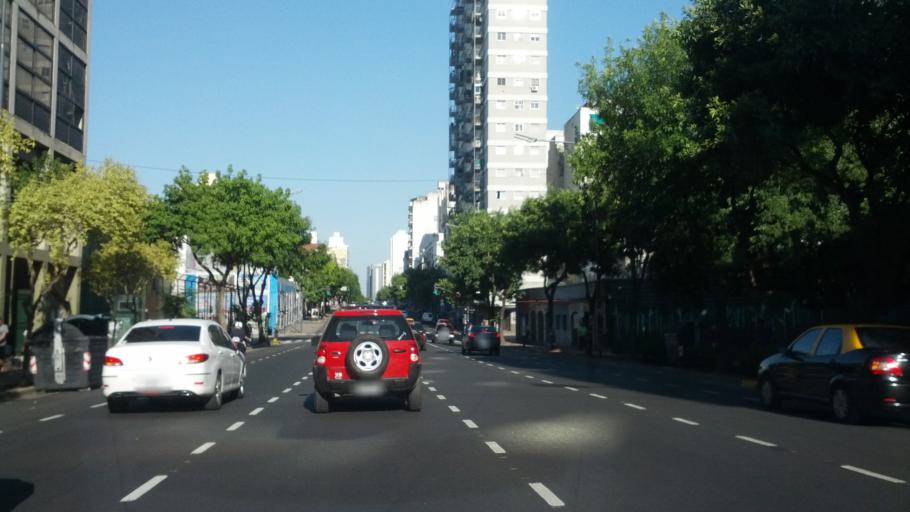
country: AR
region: Buenos Aires F.D.
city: Buenos Aires
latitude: -34.6219
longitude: -58.3753
